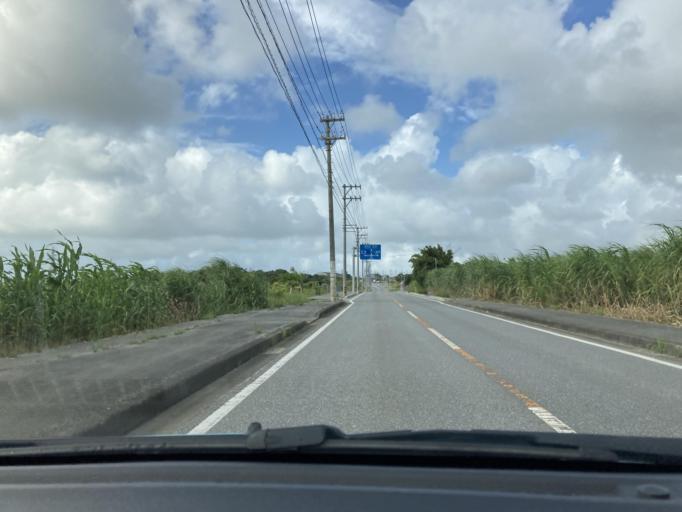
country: JP
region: Okinawa
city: Itoman
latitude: 26.1139
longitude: 127.6921
